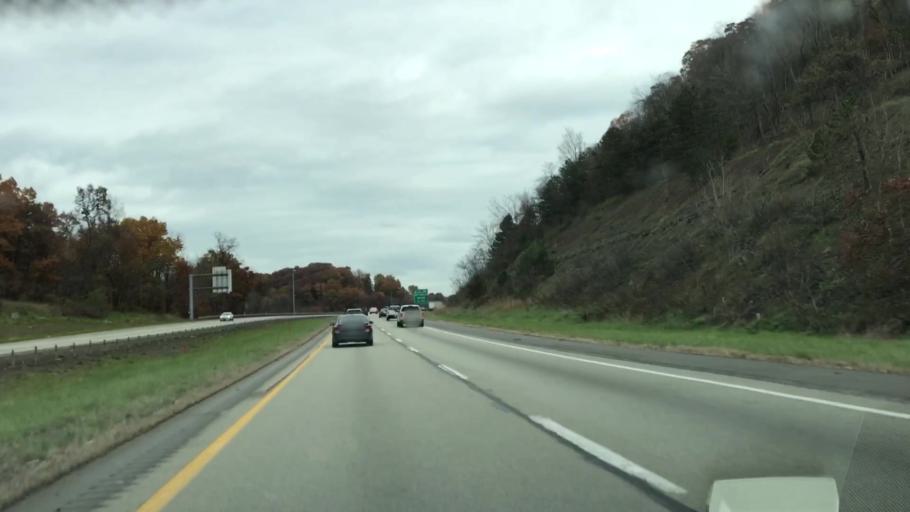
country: US
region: Pennsylvania
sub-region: Allegheny County
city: Emsworth
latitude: 40.5433
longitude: -80.1217
